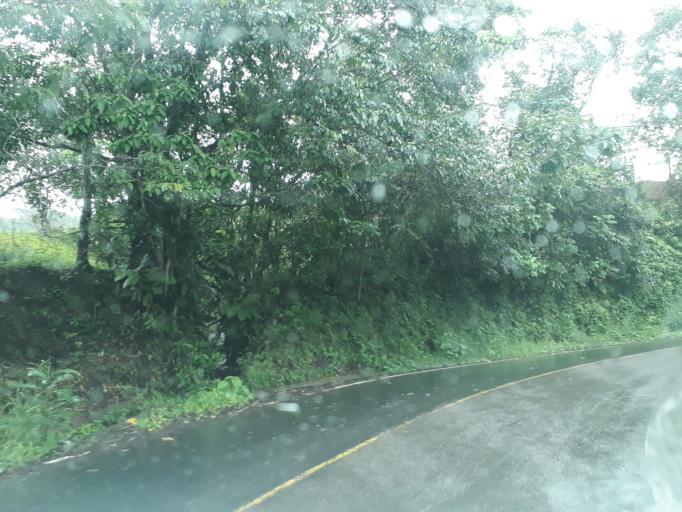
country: CO
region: Cundinamarca
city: Paratebueno
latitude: 4.4015
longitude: -73.3030
